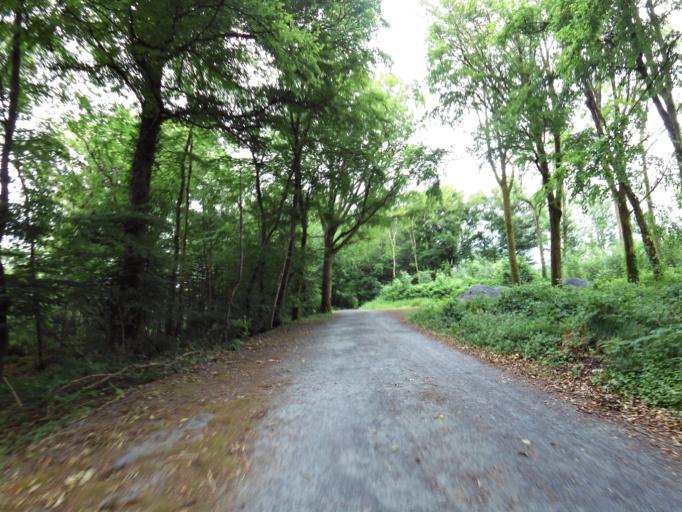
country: IE
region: Connaught
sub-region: County Galway
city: Gort
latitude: 53.0805
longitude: -8.8476
